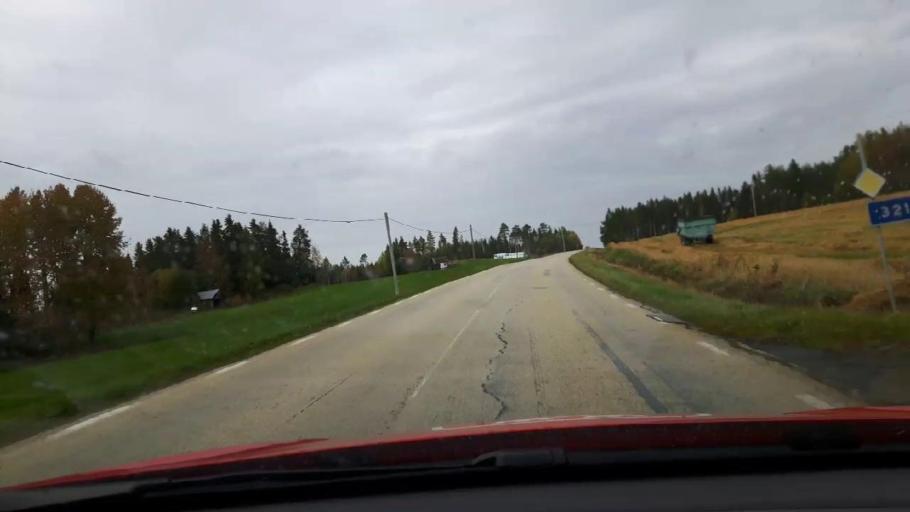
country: SE
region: Jaemtland
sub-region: Bergs Kommun
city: Hoverberg
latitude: 62.9386
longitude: 14.3343
